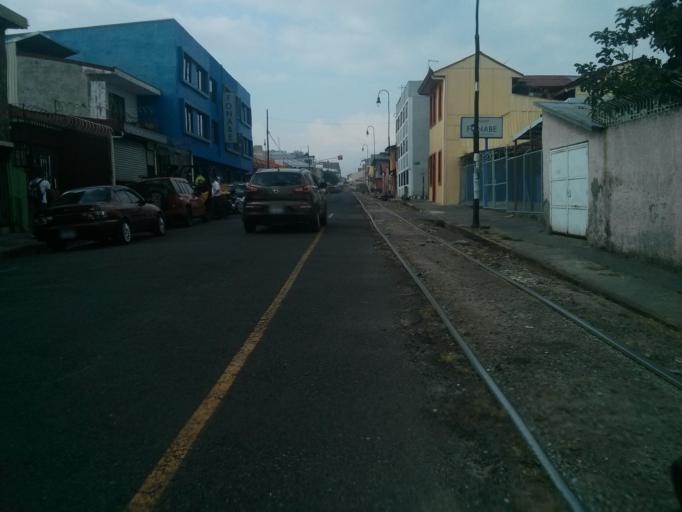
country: CR
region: San Jose
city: San Jose
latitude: 9.9284
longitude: -84.0733
